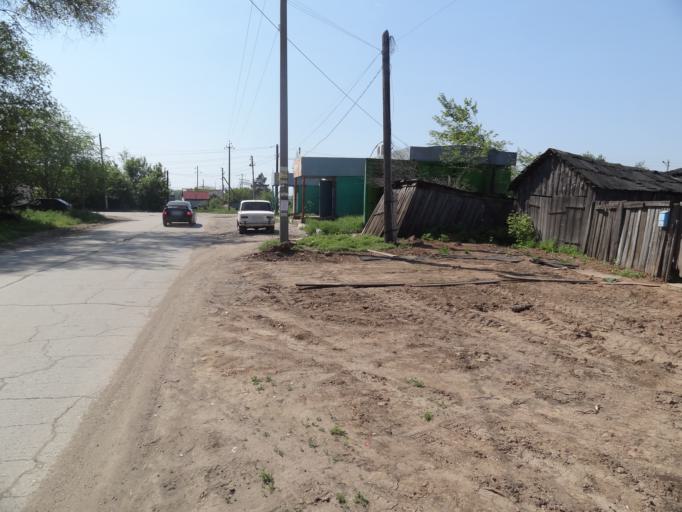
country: RU
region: Saratov
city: Privolzhskiy
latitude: 51.4084
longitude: 46.1007
